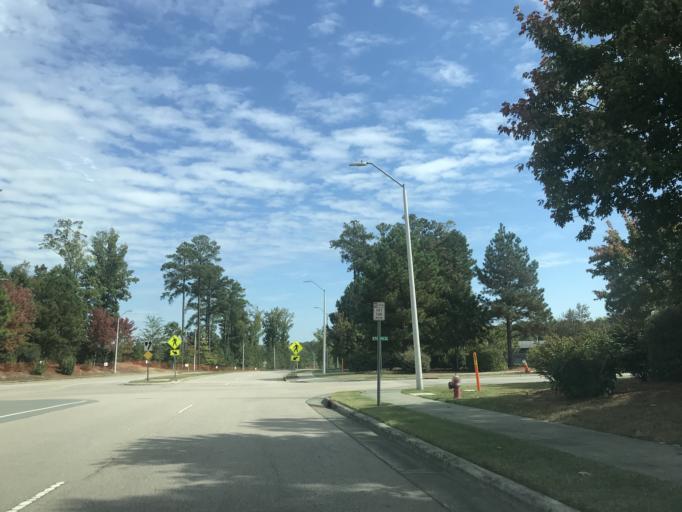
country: US
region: North Carolina
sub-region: Wake County
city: Rolesville
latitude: 35.8687
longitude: -78.5421
